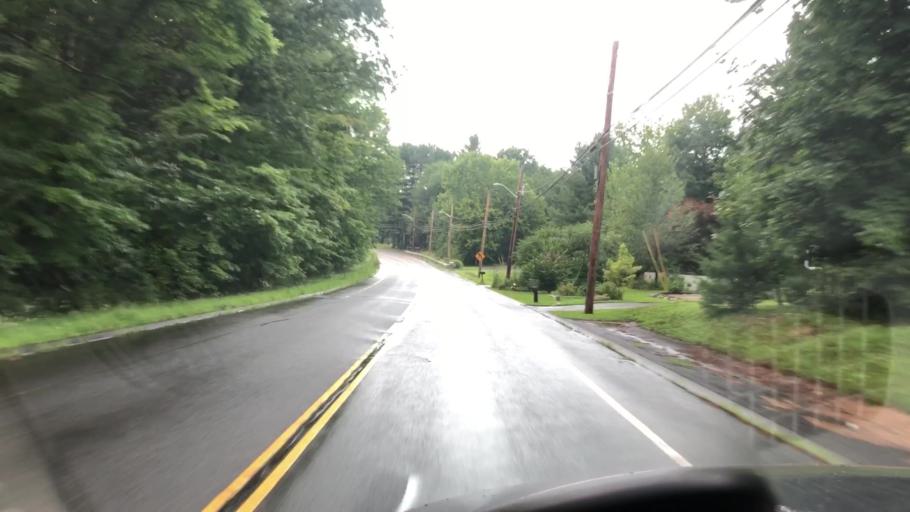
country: US
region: Massachusetts
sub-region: Hampshire County
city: Easthampton
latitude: 42.3021
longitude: -72.6828
